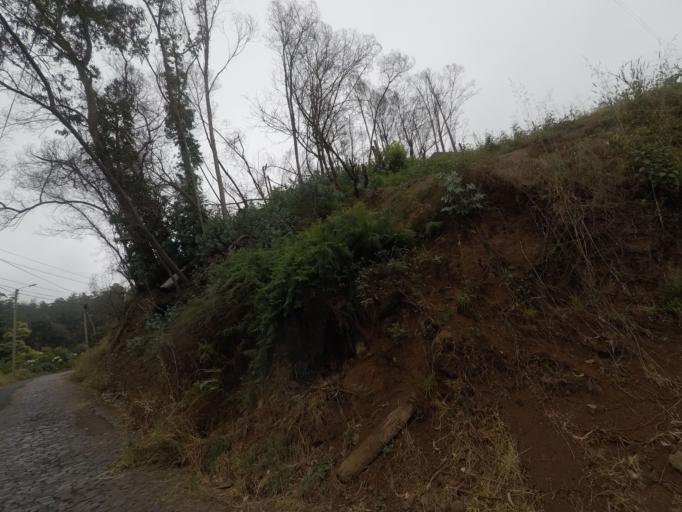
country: PT
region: Madeira
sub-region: Funchal
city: Nossa Senhora do Monte
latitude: 32.6712
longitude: -16.8860
